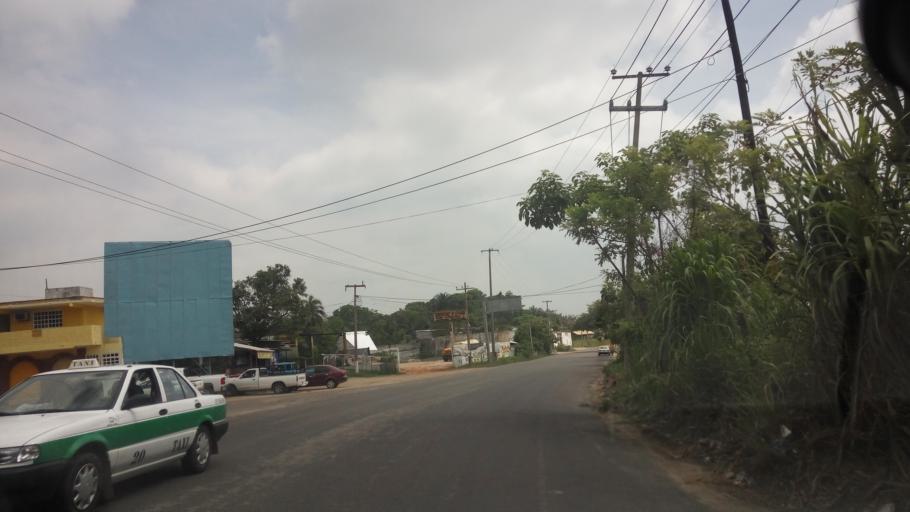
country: MX
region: Chiapas
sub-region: Reforma
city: El Carmen (El Limon)
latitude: 17.8774
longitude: -93.1512
